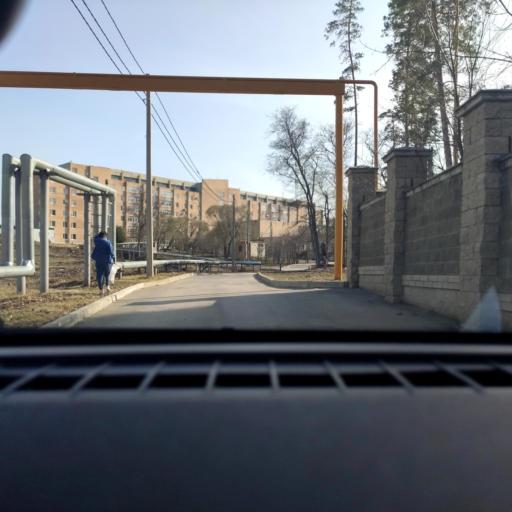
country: RU
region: Samara
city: Tol'yatti
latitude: 53.5001
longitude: 49.3587
